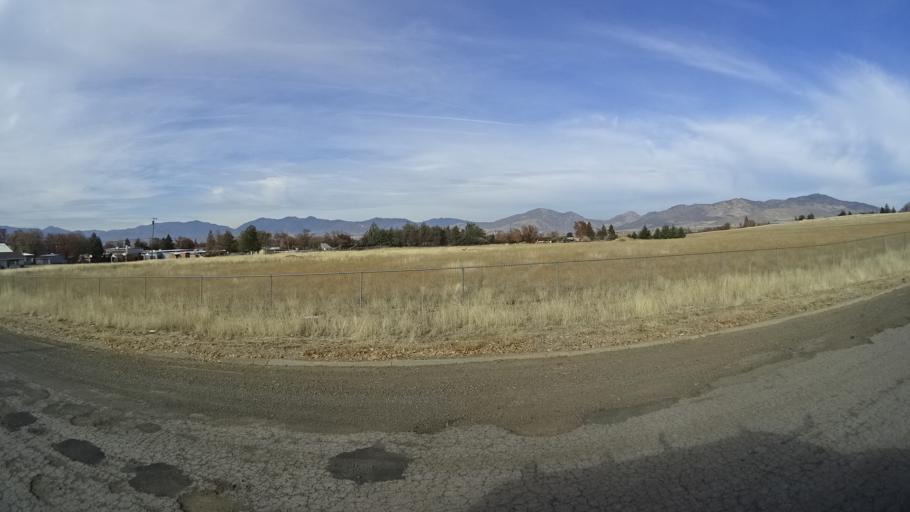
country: US
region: California
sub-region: Siskiyou County
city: Montague
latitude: 41.7283
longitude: -122.5187
